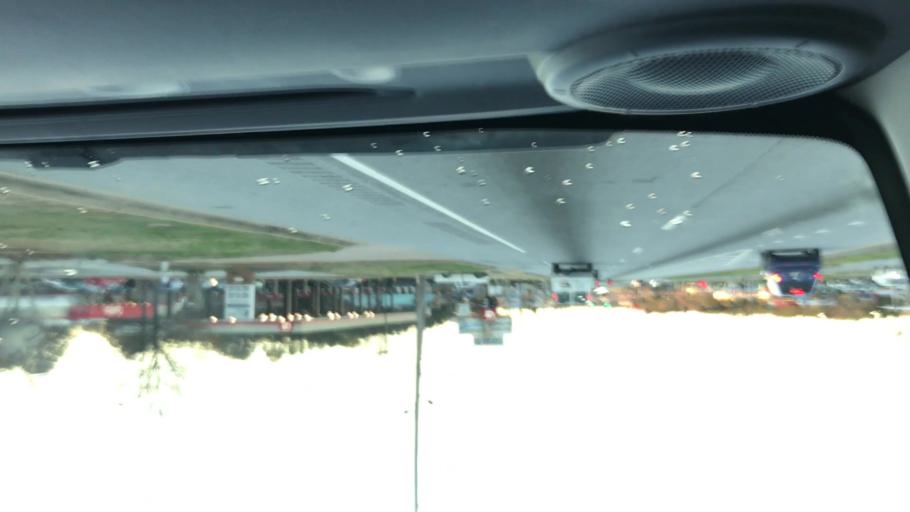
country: US
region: Georgia
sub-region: Clayton County
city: Riverdale
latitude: 33.5534
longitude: -84.4143
